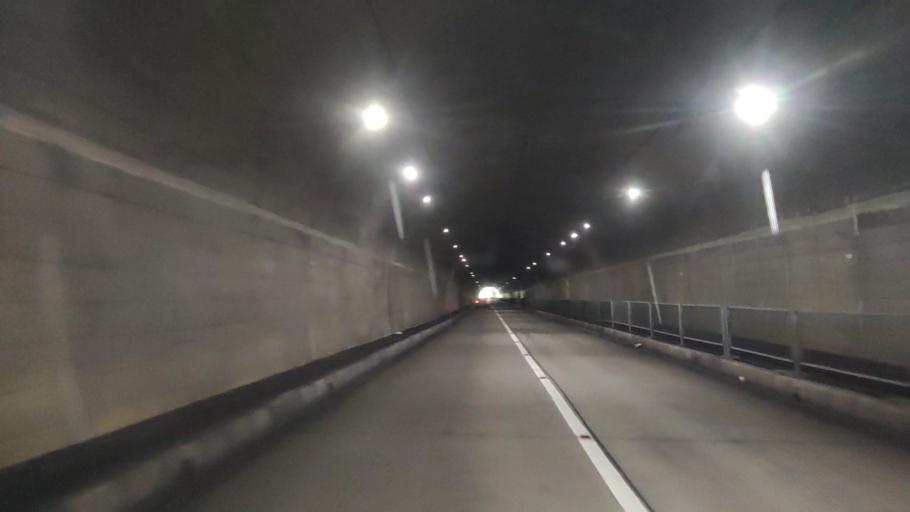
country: JP
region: Mie
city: Ise
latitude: 34.2585
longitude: 136.4788
